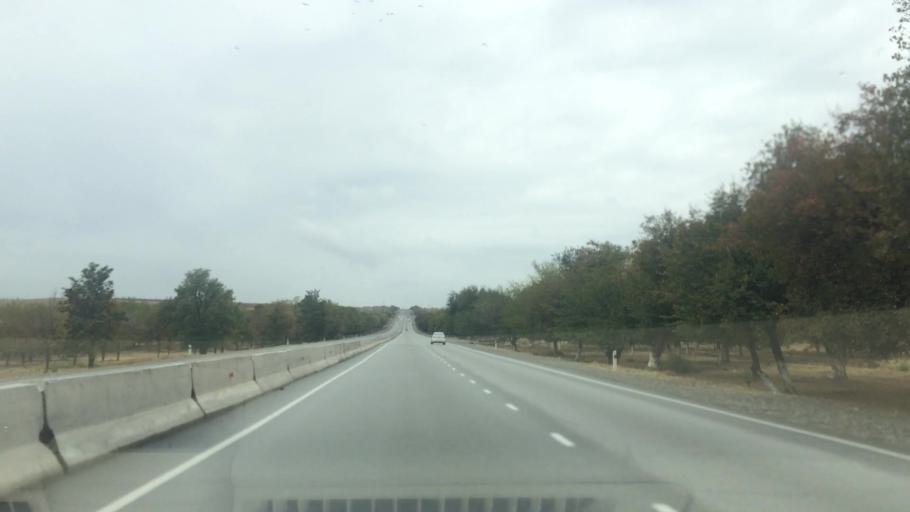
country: UZ
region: Samarqand
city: Bulung'ur
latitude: 39.8740
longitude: 67.4805
